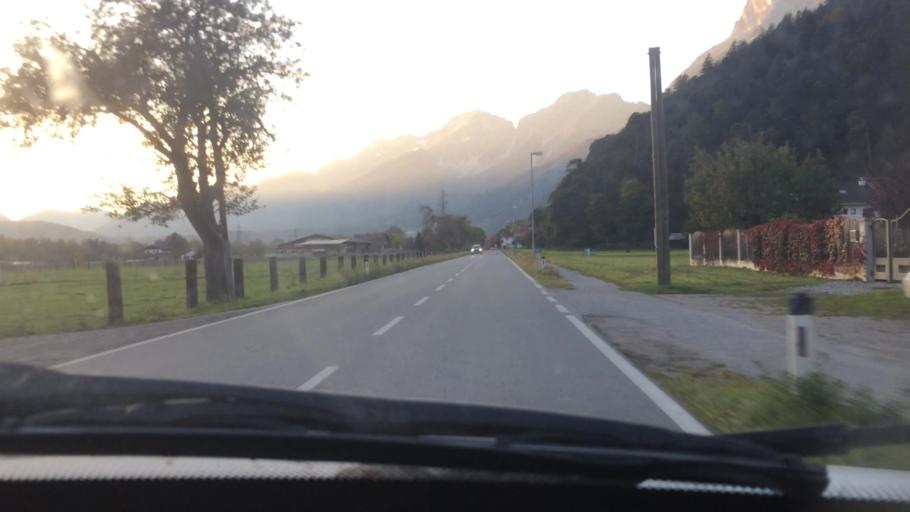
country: AT
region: Tyrol
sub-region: Politischer Bezirk Innsbruck Land
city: Pettnau
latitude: 47.2998
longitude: 11.1396
